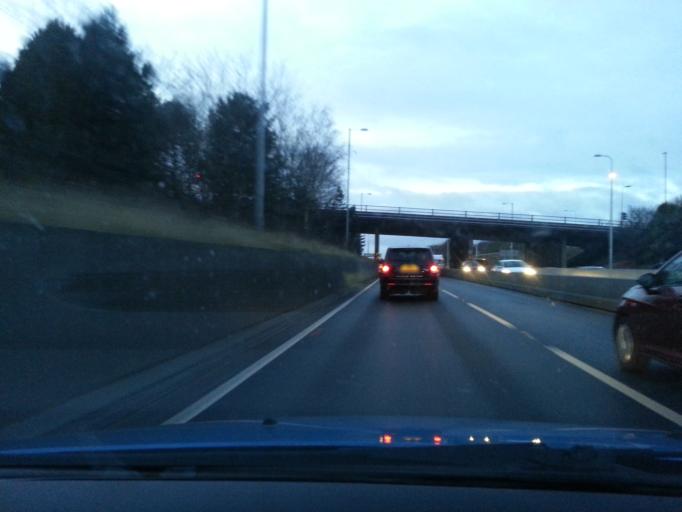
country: GB
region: England
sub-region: Gateshead
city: Whickham
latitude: 54.9508
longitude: -1.6482
